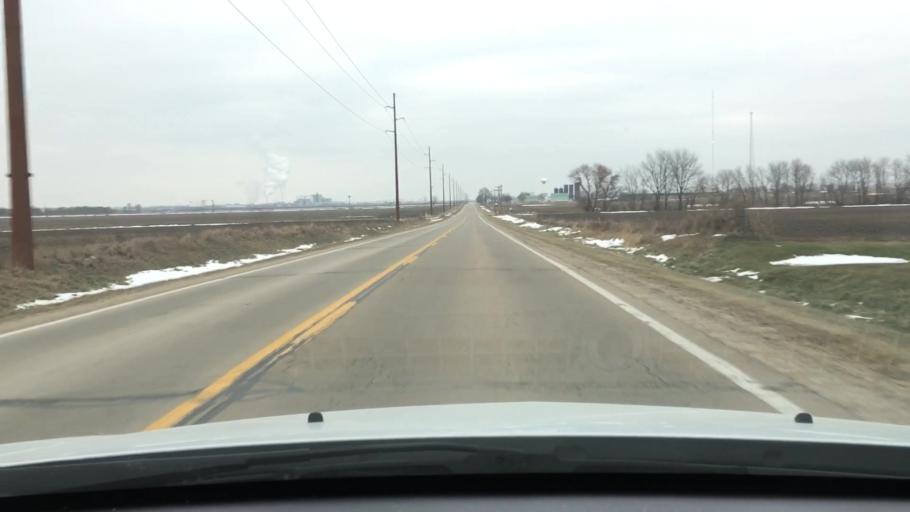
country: US
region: Illinois
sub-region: Ogle County
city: Rochelle
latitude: 41.8597
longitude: -89.0248
